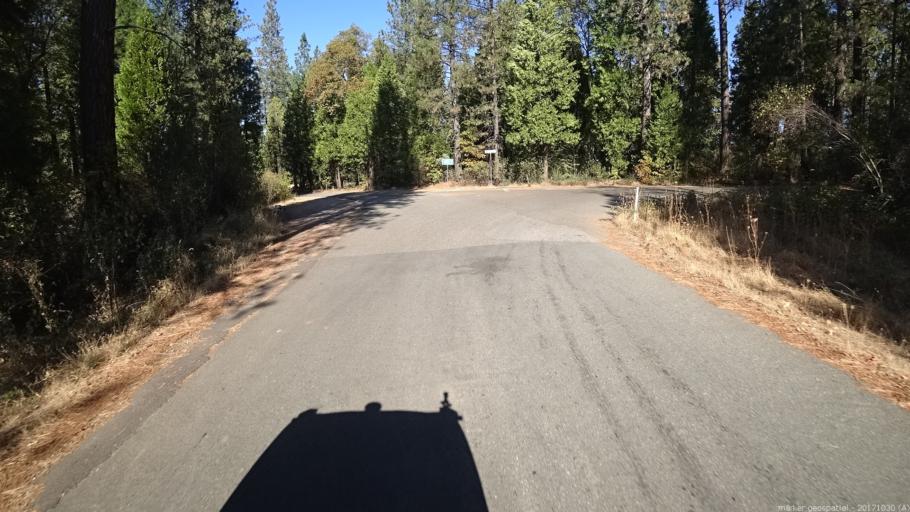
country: US
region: California
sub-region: Shasta County
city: Shingletown
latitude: 40.5291
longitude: -121.9272
